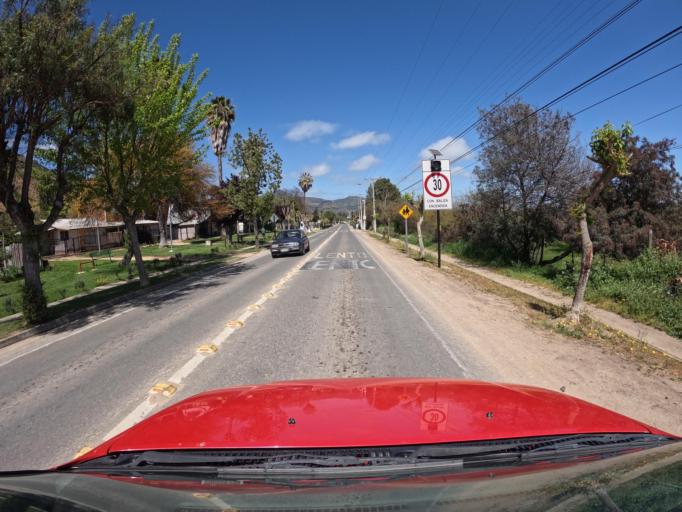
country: CL
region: O'Higgins
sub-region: Provincia de Colchagua
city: Santa Cruz
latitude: -34.7229
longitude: -71.6392
